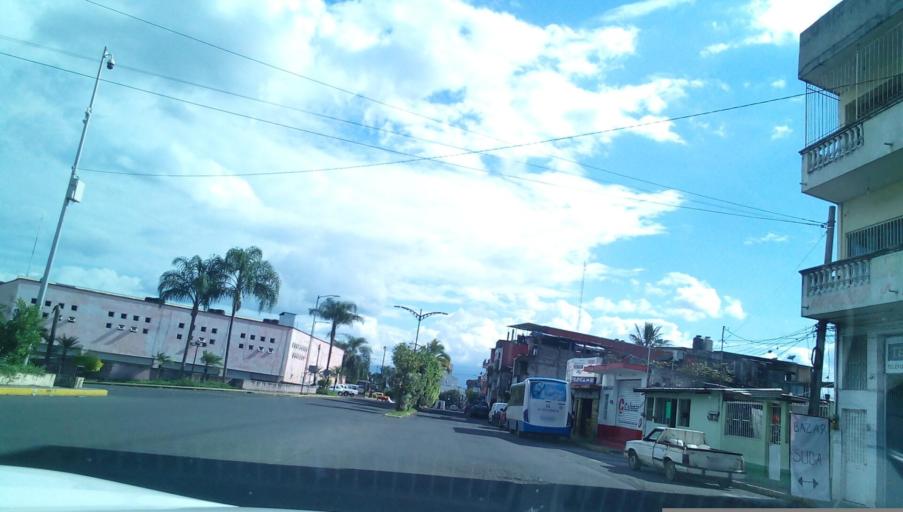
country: MX
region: Veracruz
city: Cordoba
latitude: 18.8868
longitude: -96.9221
